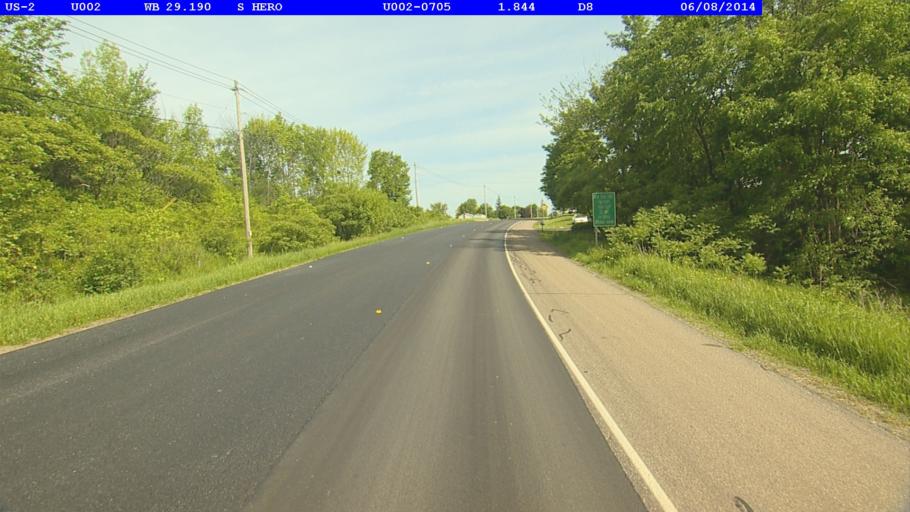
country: US
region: New York
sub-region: Clinton County
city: Cumberland Head
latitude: 44.6547
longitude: -73.3201
